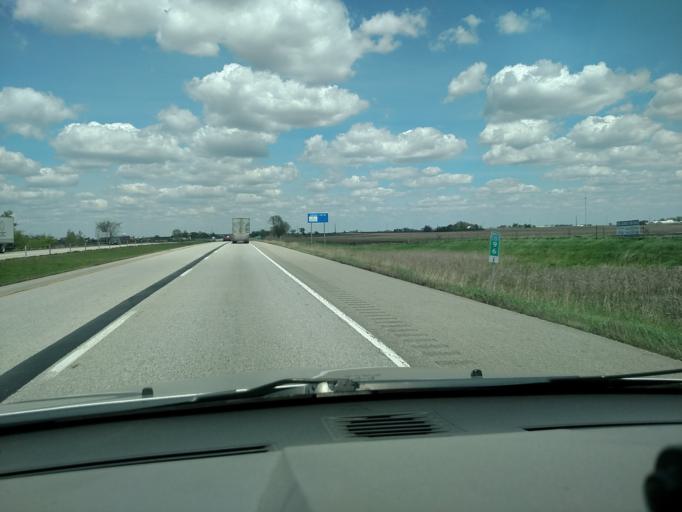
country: US
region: Iowa
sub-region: Polk County
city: Ankeny
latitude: 41.7807
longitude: -93.5706
